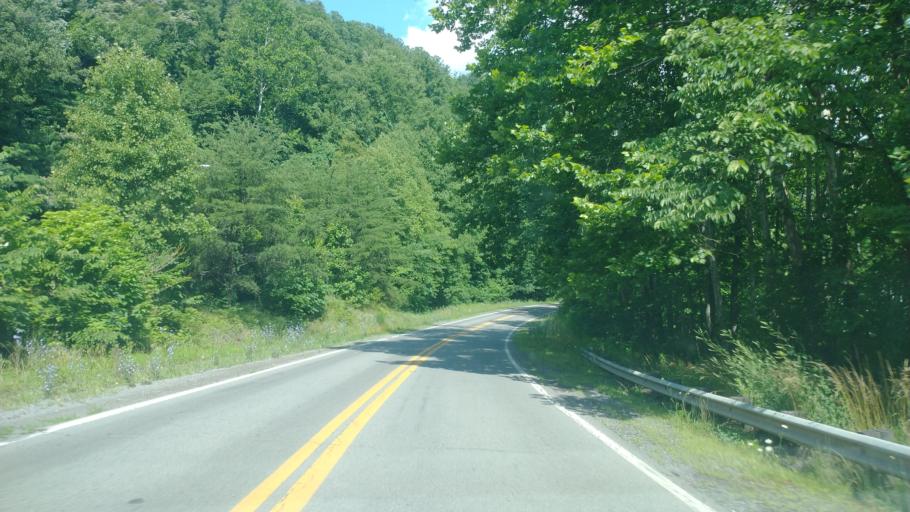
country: US
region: West Virginia
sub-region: McDowell County
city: Welch
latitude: 37.4240
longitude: -81.5488
